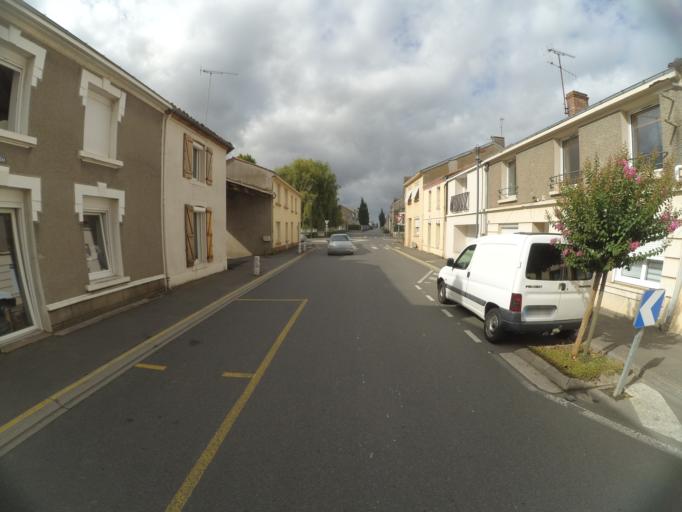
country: FR
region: Pays de la Loire
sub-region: Departement de Maine-et-Loire
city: Villedieu-la-Blouere
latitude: 47.1467
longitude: -1.0641
